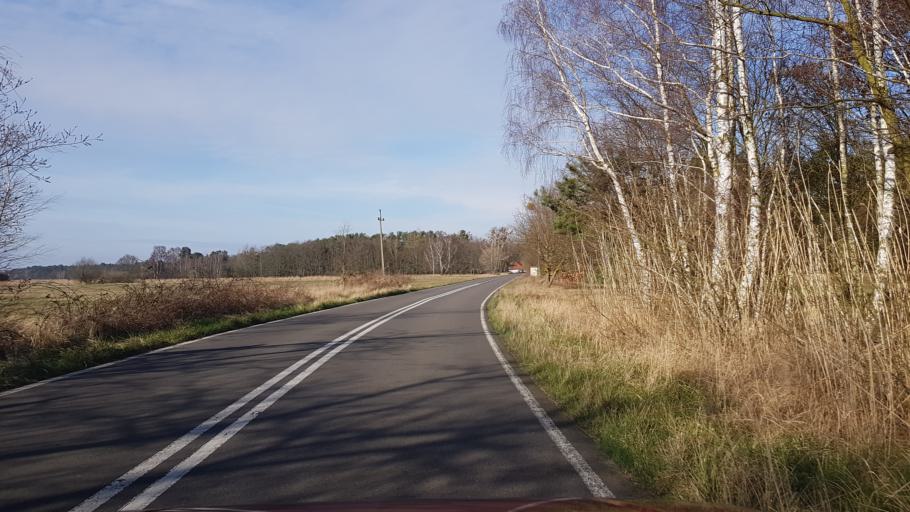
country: PL
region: West Pomeranian Voivodeship
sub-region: Powiat policki
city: Nowe Warpno
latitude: 53.7307
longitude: 14.3098
